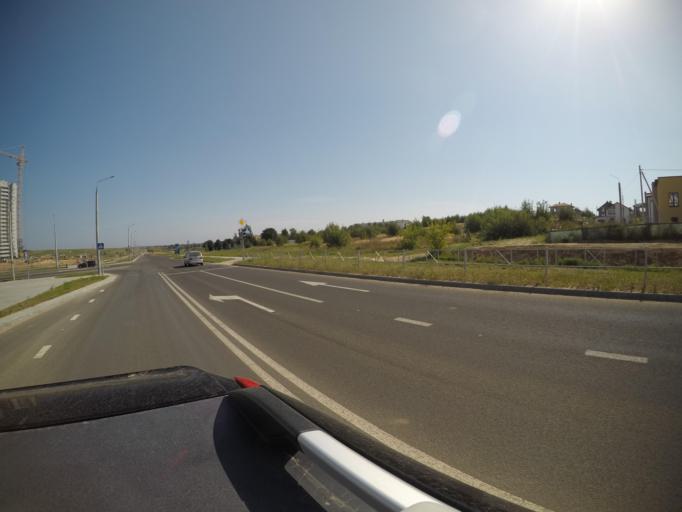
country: BY
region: Grodnenskaya
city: Hrodna
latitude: 53.7183
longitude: 23.8823
